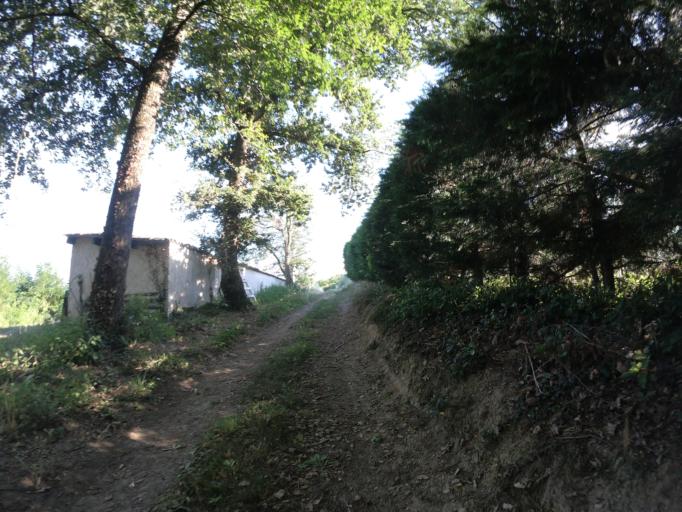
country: FR
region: Midi-Pyrenees
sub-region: Departement de l'Ariege
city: La Tour-du-Crieu
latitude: 43.1012
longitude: 1.7145
